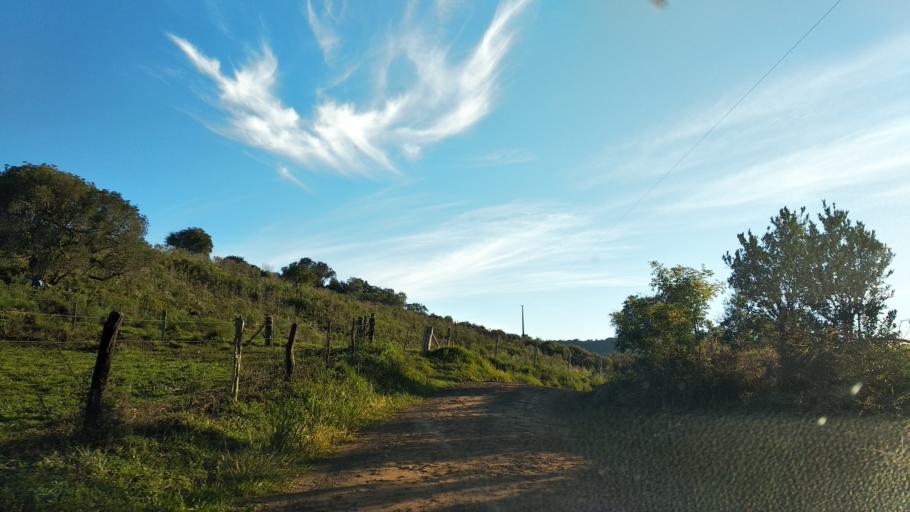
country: BR
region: Santa Catarina
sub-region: Celso Ramos
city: Celso Ramos
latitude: -27.5596
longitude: -51.2295
